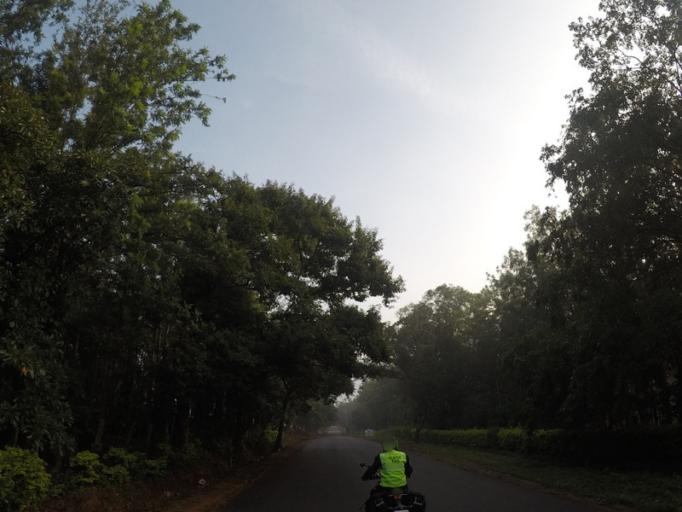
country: IN
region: Karnataka
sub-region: Chikmagalur
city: Chikmagalur
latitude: 13.4109
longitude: 75.7970
